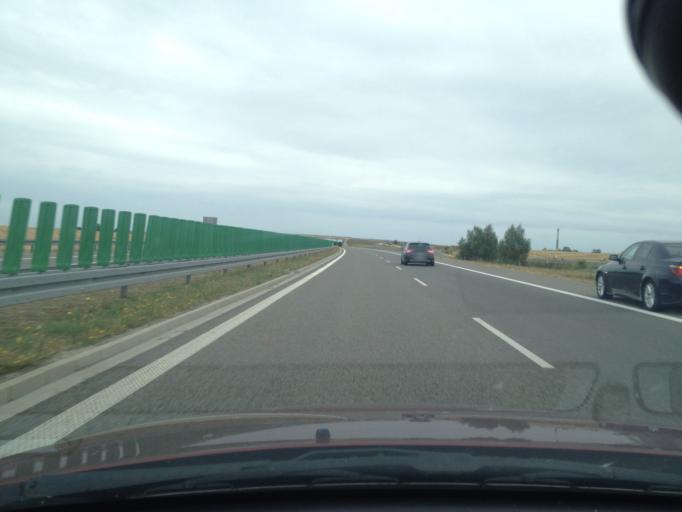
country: PL
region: Lubusz
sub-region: Powiat gorzowski
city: Jenin
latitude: 52.7669
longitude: 15.1302
